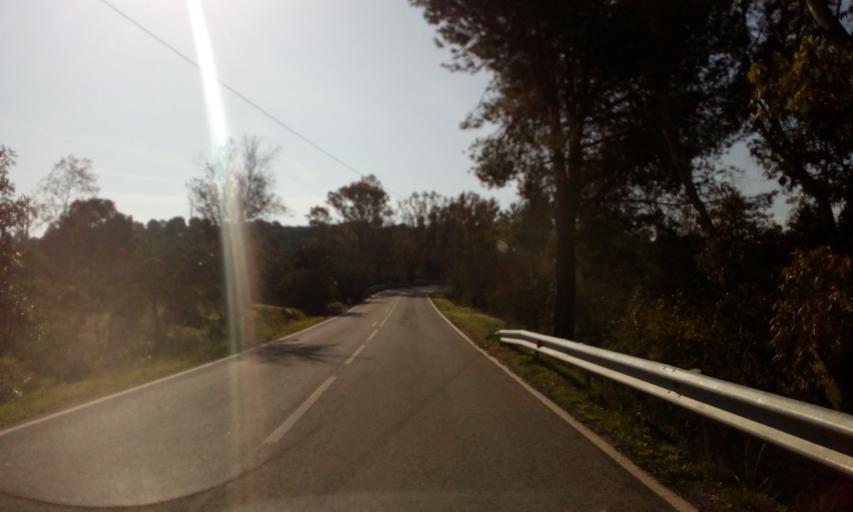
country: PT
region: Faro
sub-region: Alcoutim
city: Alcoutim
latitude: 37.4561
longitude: -7.4838
